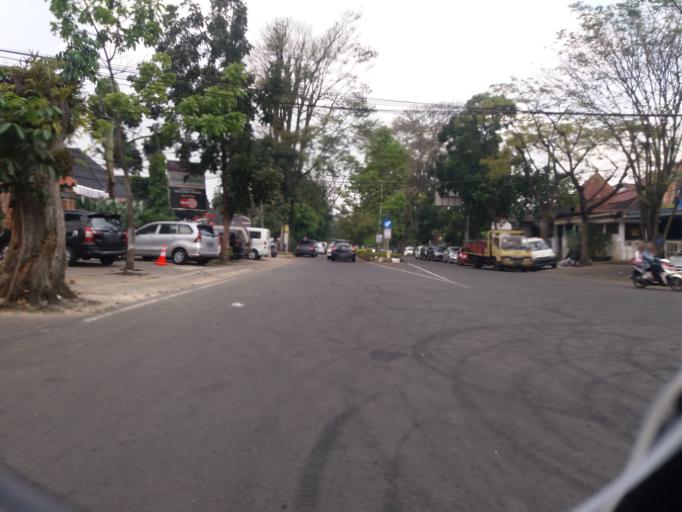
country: ID
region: West Java
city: Bandung
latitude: -6.9014
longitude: 107.6252
